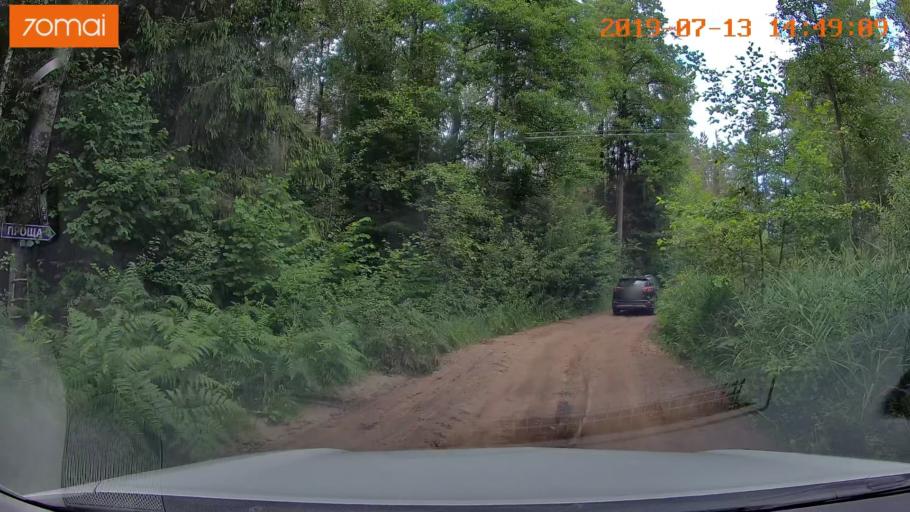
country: BY
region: Mogilev
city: Asipovichy
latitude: 53.2063
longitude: 28.7469
